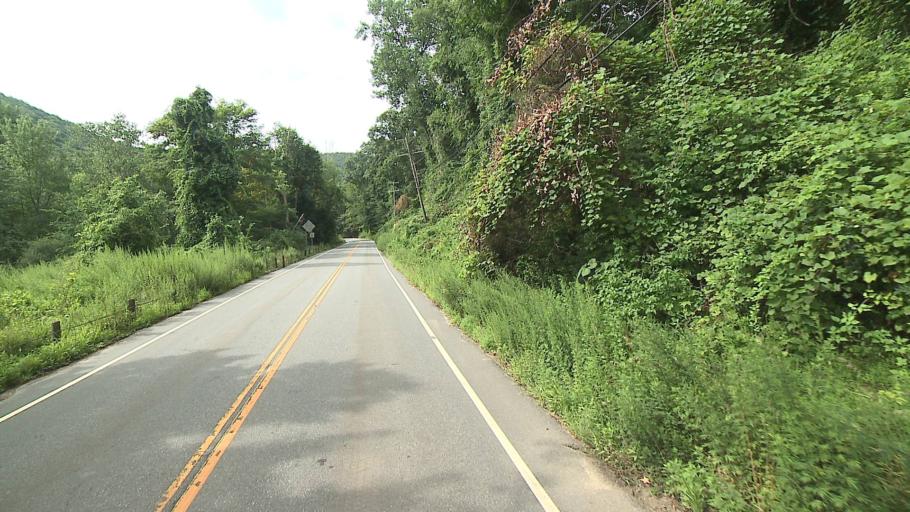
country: US
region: Connecticut
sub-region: Litchfield County
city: Kent
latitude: 41.7174
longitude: -73.4598
